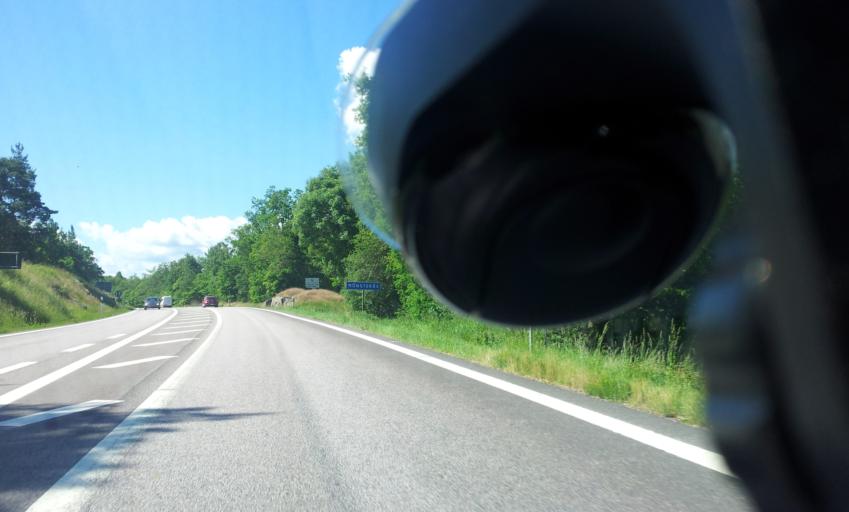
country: SE
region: Kalmar
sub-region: Monsteras Kommun
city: Moensteras
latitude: 57.0595
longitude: 16.4435
